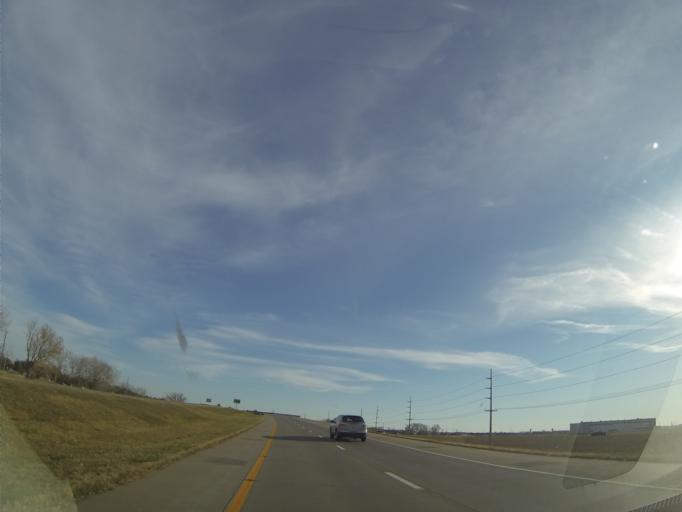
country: US
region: Kansas
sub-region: Saline County
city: Salina
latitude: 38.8142
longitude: -97.6344
